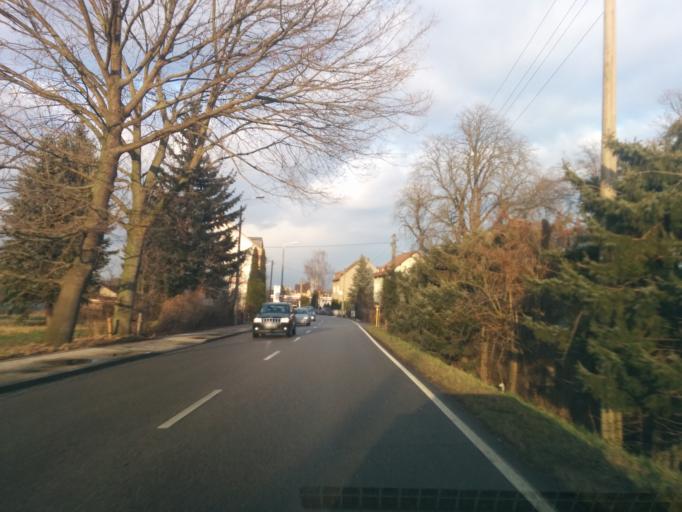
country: DE
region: Saxony
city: Frankenberg
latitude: 50.9048
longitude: 13.0196
